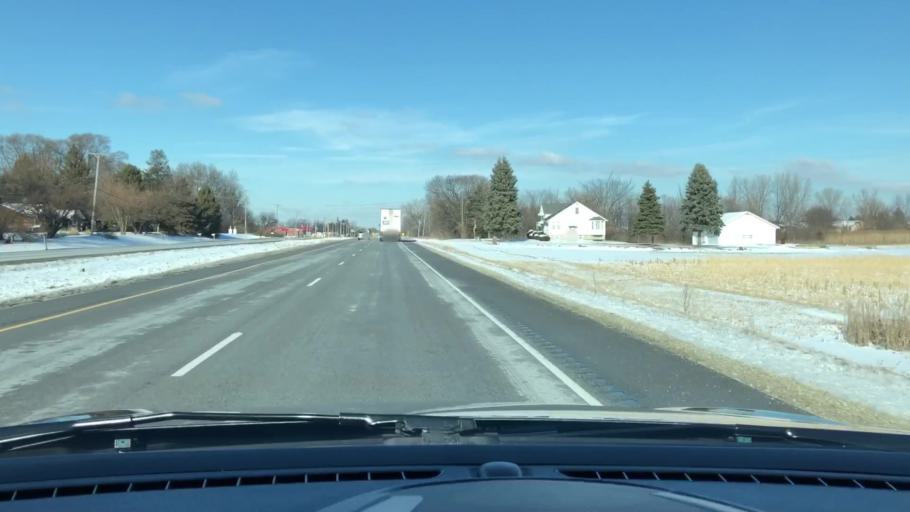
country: US
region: Illinois
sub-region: Will County
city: Preston Heights
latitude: 41.4742
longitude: -88.0798
